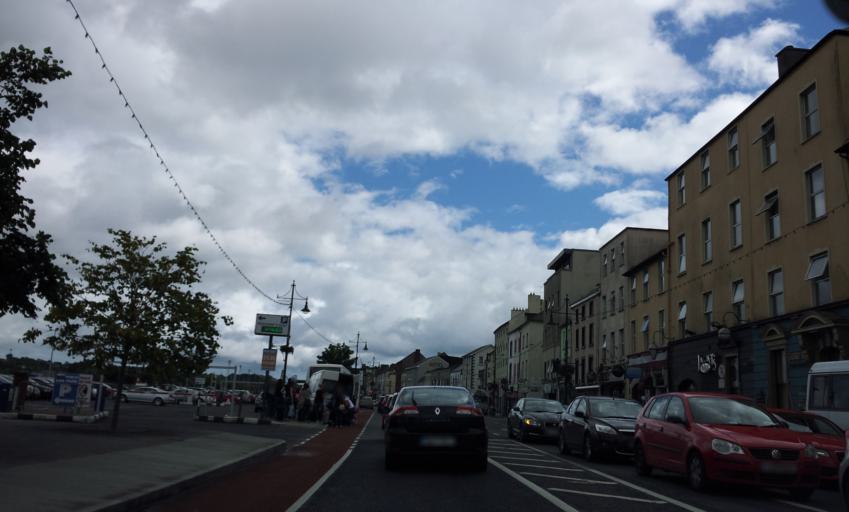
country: IE
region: Munster
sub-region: Waterford
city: Waterford
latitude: 52.2639
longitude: -7.1185
